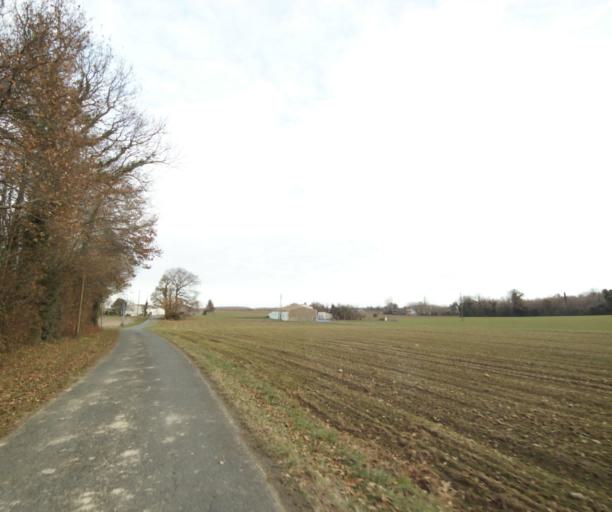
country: FR
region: Poitou-Charentes
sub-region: Departement de la Charente-Maritime
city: Corme-Royal
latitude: 45.7828
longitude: -0.8255
